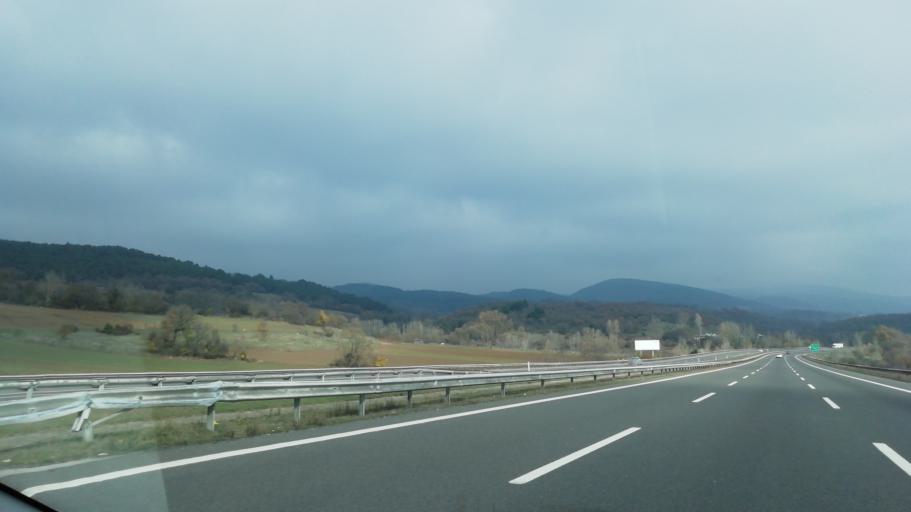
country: TR
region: Bolu
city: Bolu
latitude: 40.7359
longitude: 31.5341
